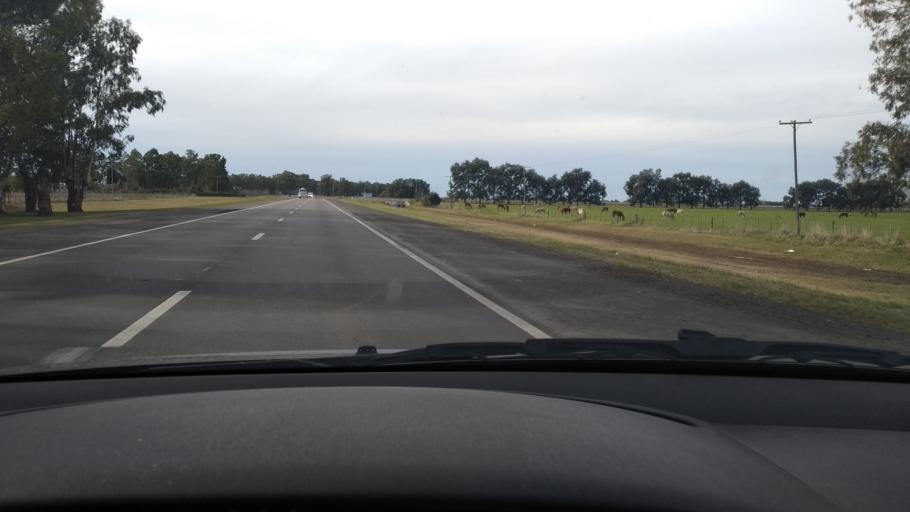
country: AR
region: Buenos Aires
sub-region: Partido de Azul
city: Azul
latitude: -36.7697
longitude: -59.8140
